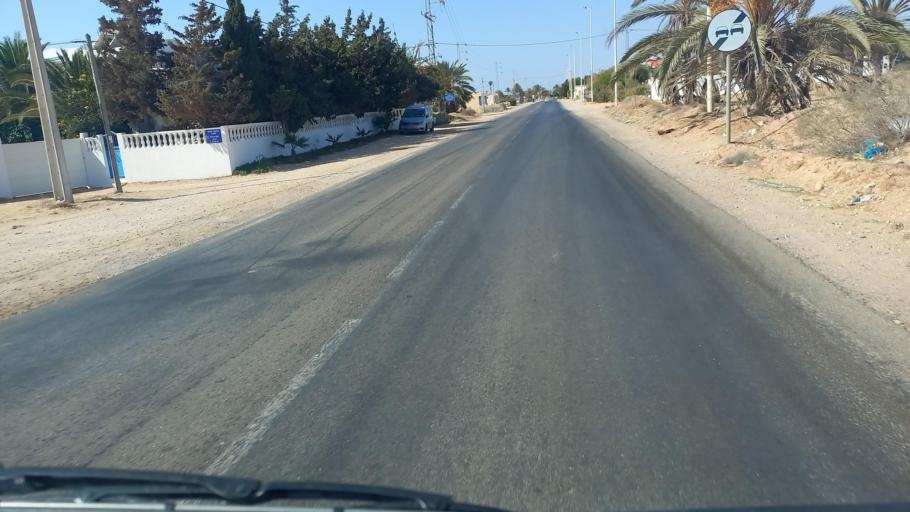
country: TN
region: Madanin
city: Midoun
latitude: 33.7743
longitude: 11.0284
